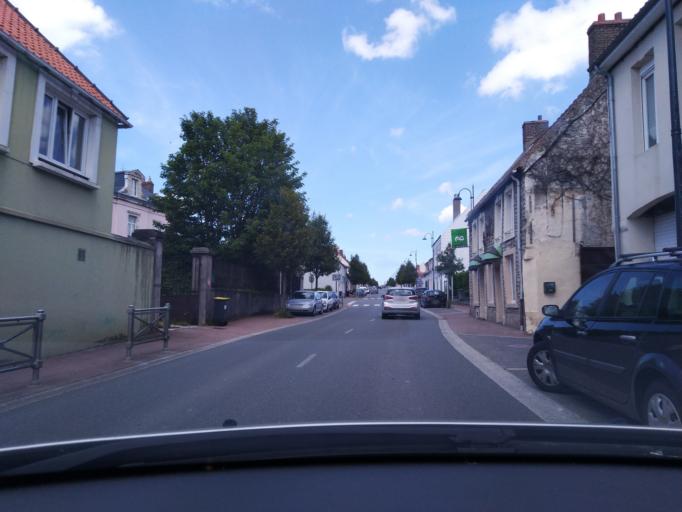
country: FR
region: Nord-Pas-de-Calais
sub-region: Departement du Pas-de-Calais
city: Marquise
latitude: 50.8152
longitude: 1.7017
